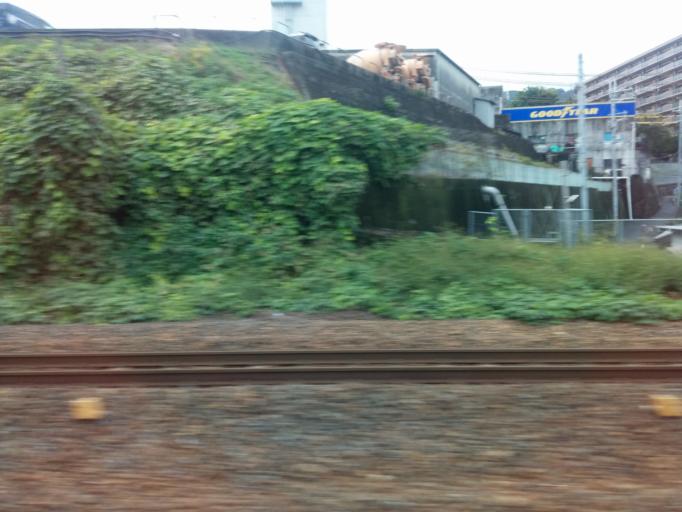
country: JP
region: Shiga Prefecture
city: Otsu-shi
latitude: 35.0020
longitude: 135.8753
